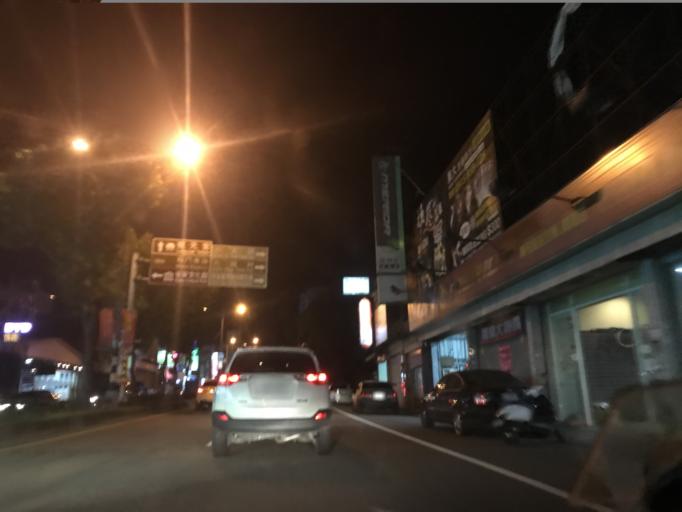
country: TW
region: Taiwan
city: Daxi
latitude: 24.8714
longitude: 121.2137
